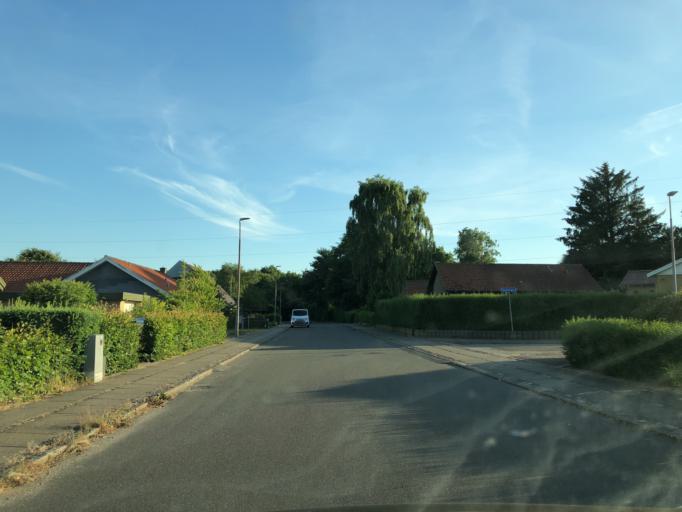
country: DK
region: Central Jutland
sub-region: Struer Kommune
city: Struer
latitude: 56.4833
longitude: 8.5853
